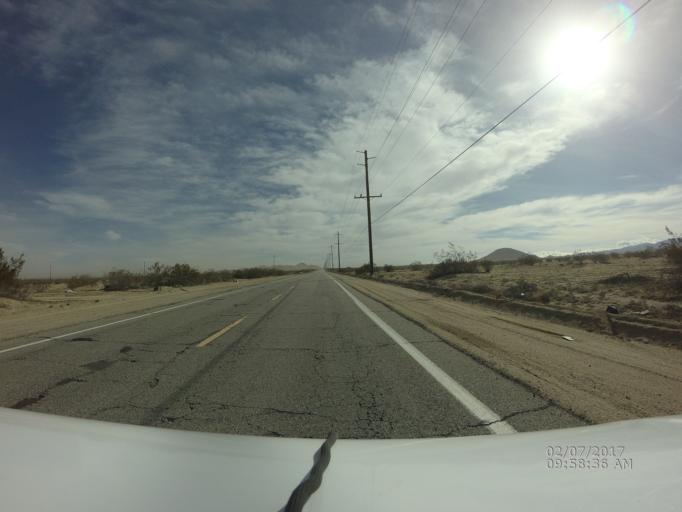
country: US
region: California
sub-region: Los Angeles County
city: Lake Los Angeles
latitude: 34.5799
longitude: -117.7621
